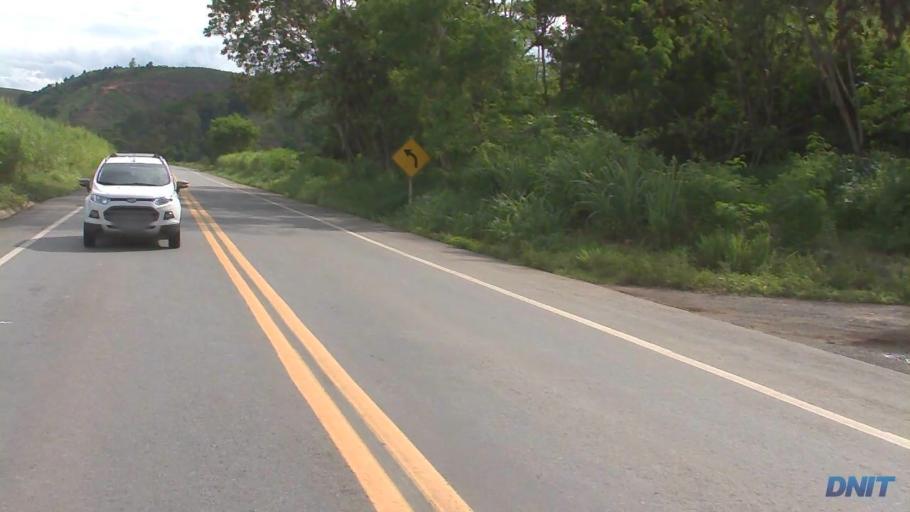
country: BR
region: Minas Gerais
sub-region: Belo Oriente
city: Belo Oriente
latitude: -19.2708
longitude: -42.3566
